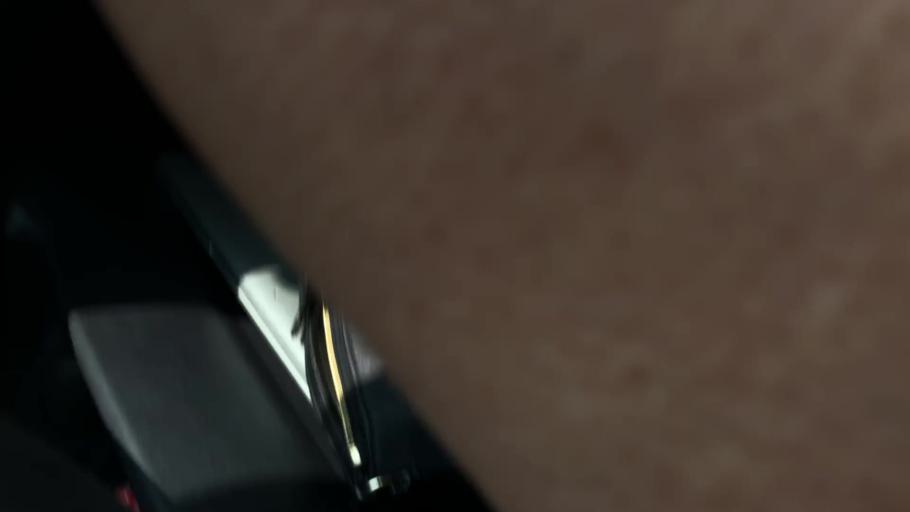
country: US
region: California
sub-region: El Dorado County
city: South Lake Tahoe
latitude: 38.8238
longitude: -120.0607
